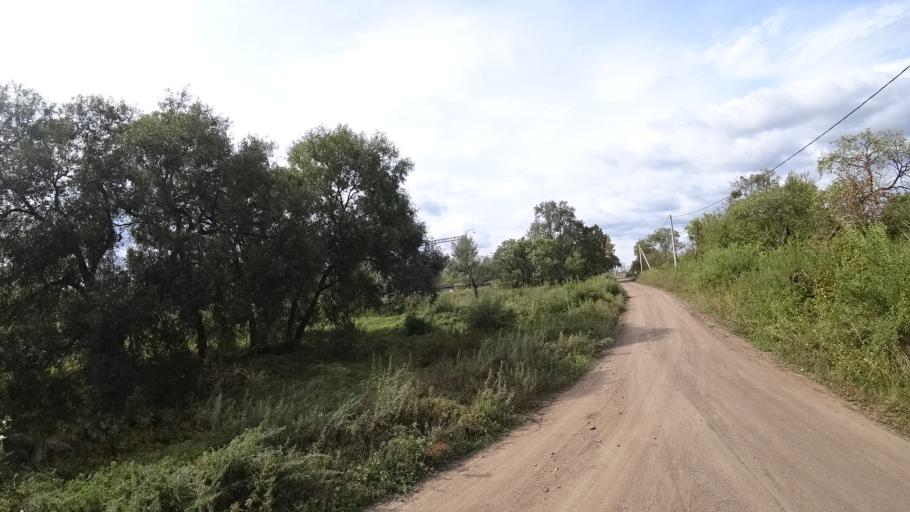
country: RU
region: Amur
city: Arkhara
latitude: 49.3480
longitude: 130.1621
